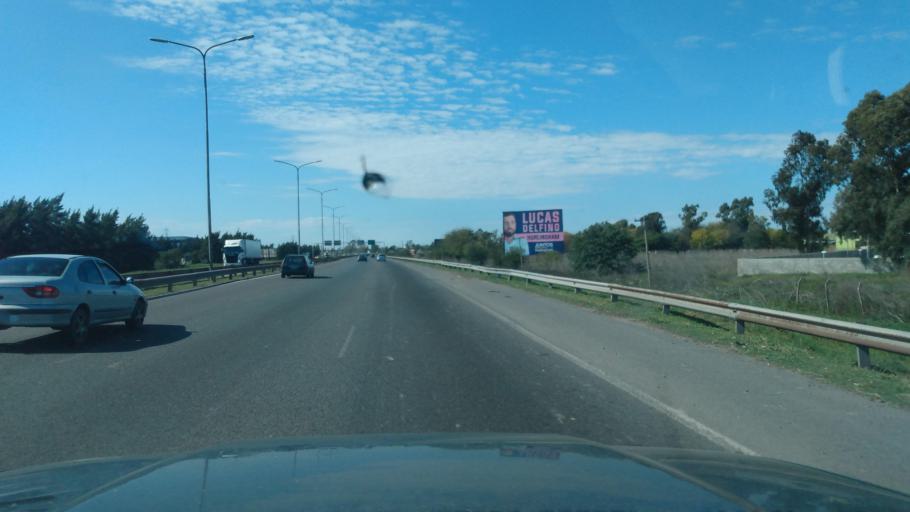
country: AR
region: Buenos Aires
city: Hurlingham
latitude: -34.5519
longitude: -58.6204
